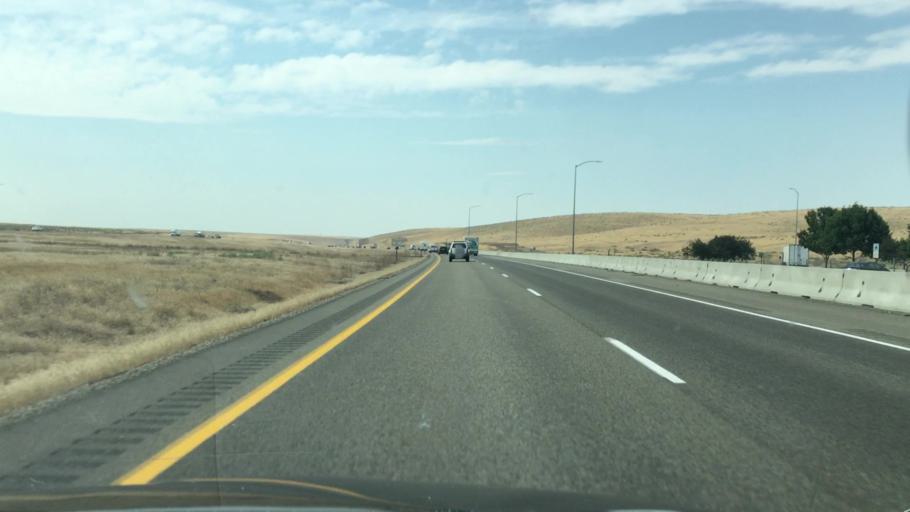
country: US
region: Idaho
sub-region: Ada County
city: Boise
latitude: 43.4790
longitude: -116.1066
